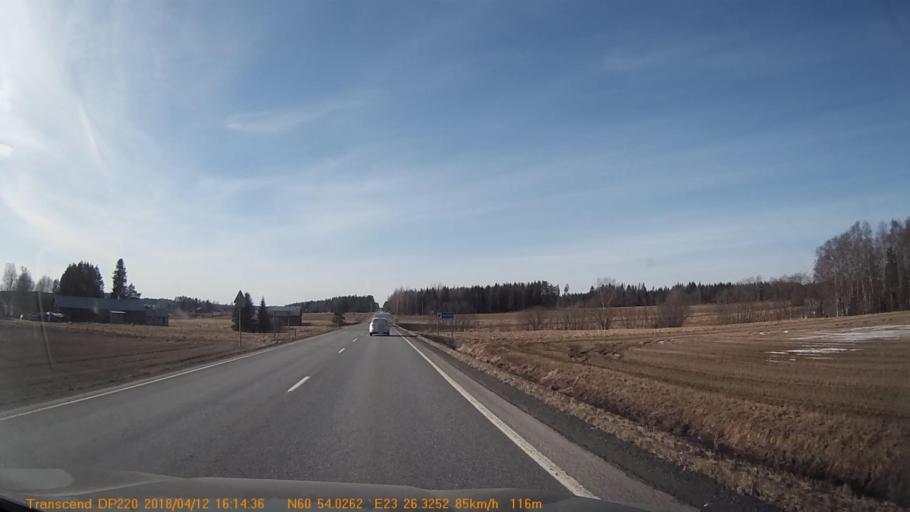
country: FI
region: Haeme
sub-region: Forssa
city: Humppila
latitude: 60.9006
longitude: 23.4390
